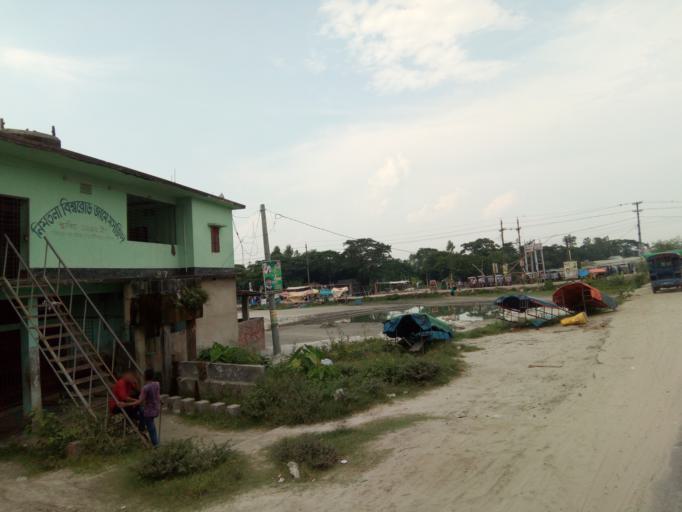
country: BD
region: Dhaka
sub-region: Dhaka
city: Dhaka
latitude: 23.6151
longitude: 90.3319
